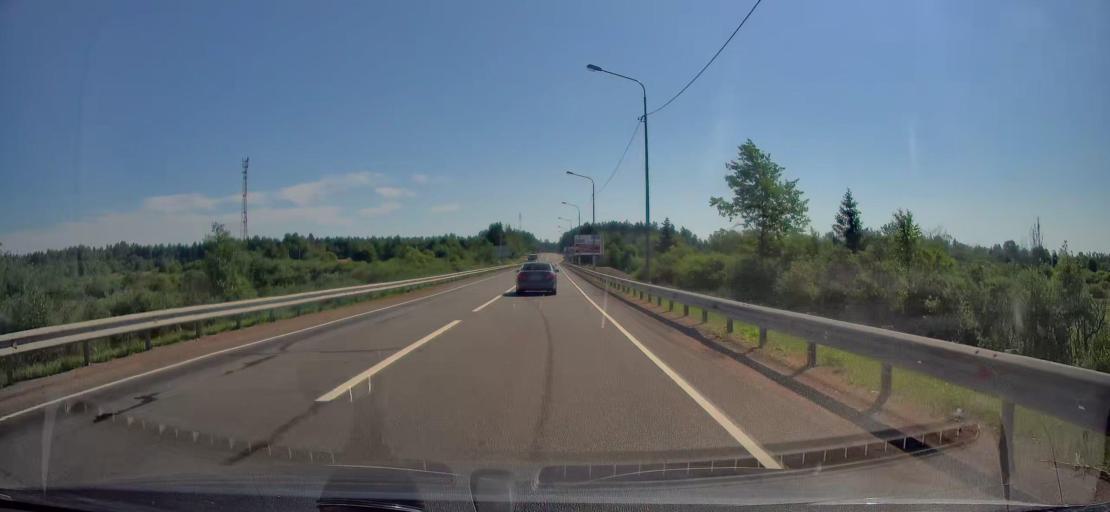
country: RU
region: Leningrad
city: Yefimovskiy
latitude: 59.3468
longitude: 34.8505
